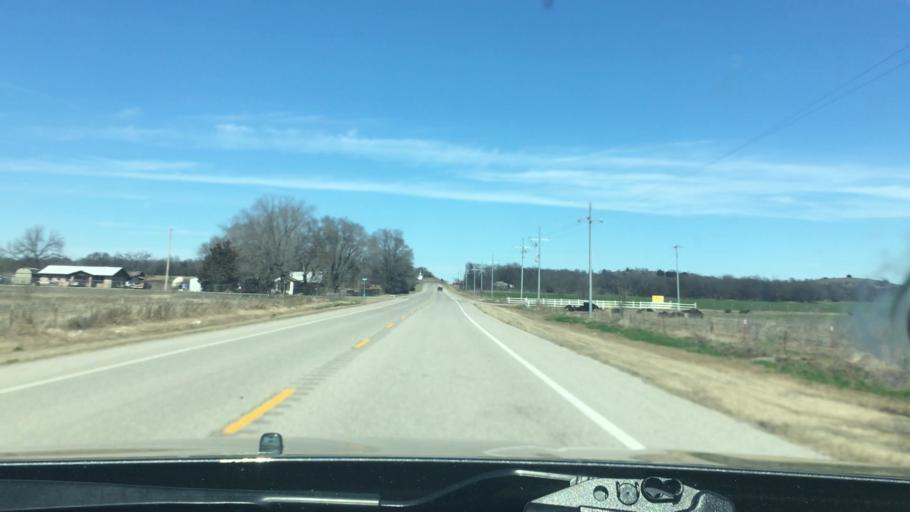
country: US
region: Oklahoma
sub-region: Murray County
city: Sulphur
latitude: 34.3964
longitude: -96.9510
